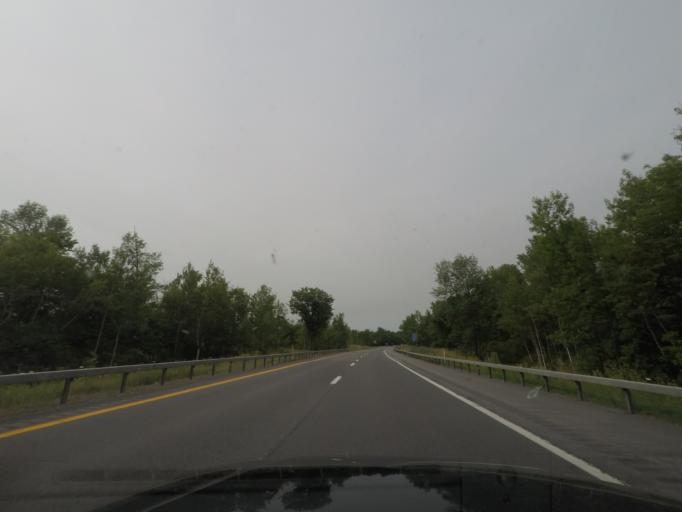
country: US
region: New York
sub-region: Clinton County
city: Champlain
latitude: 44.8956
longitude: -73.4544
